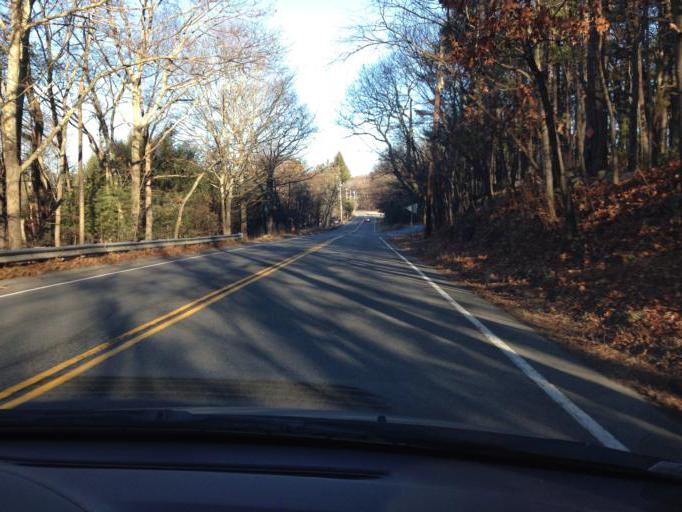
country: US
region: Massachusetts
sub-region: Middlesex County
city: Bedford
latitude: 42.5157
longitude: -71.2847
